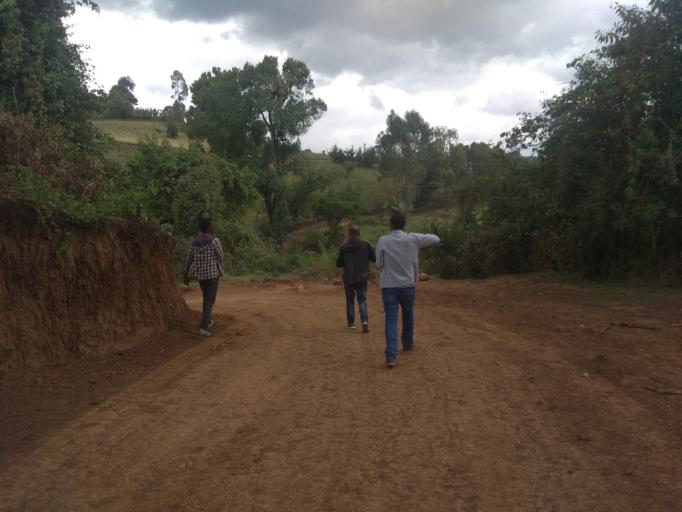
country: ET
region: Oromiya
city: Guder
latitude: 8.7489
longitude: 37.6304
